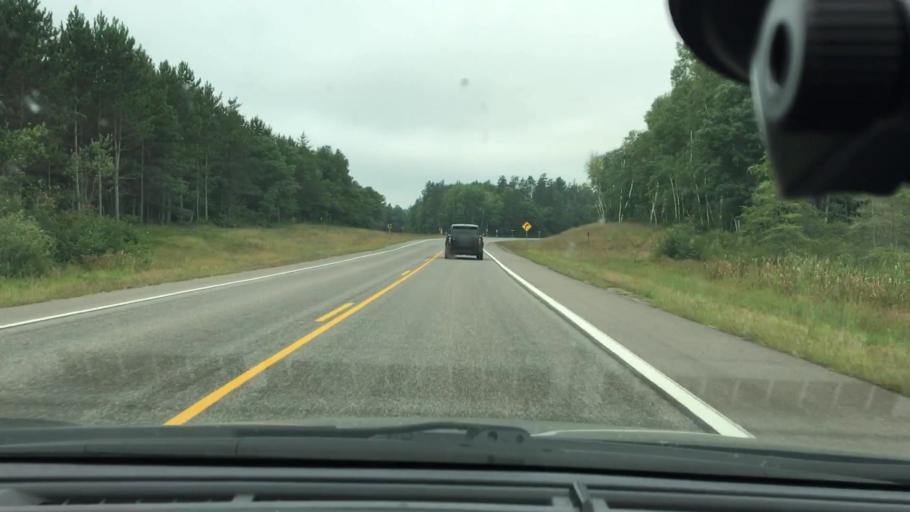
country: US
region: Minnesota
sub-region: Crow Wing County
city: Cross Lake
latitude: 46.6602
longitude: -94.0306
